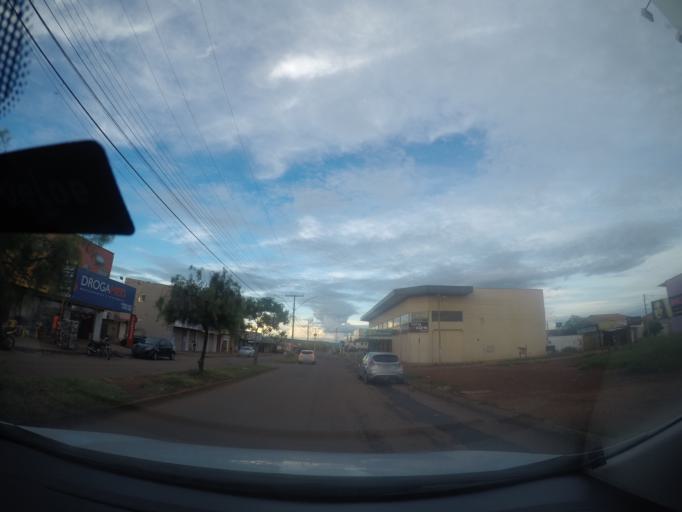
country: BR
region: Goias
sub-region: Goianira
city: Goianira
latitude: -16.5764
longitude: -49.3863
